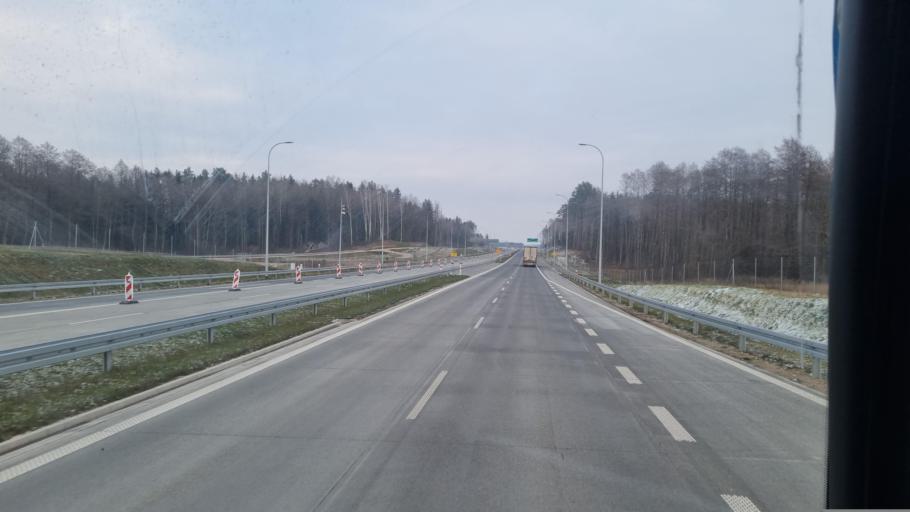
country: PL
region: Podlasie
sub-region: Powiat grajewski
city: Rajgrod
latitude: 53.8578
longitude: 22.5870
